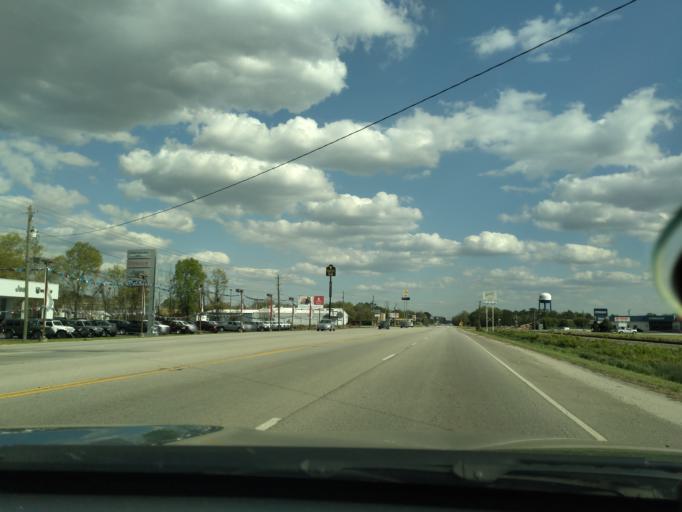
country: US
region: South Carolina
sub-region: Florence County
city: Florence
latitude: 34.2254
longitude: -79.7941
